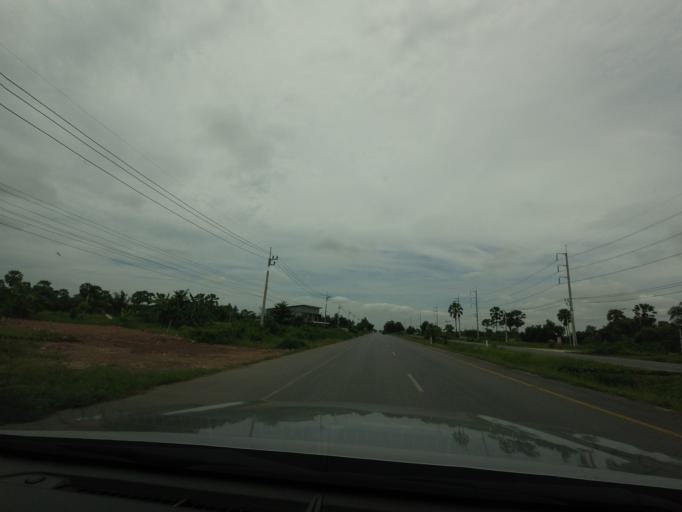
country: TH
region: Nakhon Si Thammarat
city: Hua Sai
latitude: 8.0428
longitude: 100.2875
